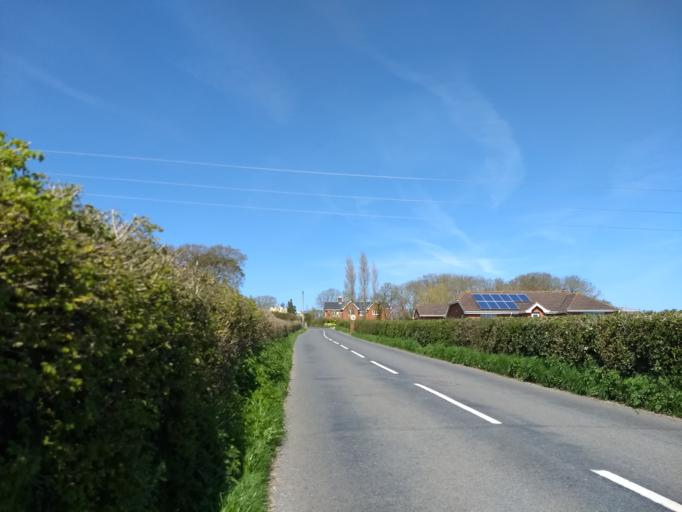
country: GB
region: England
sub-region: Isle of Wight
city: Northwood
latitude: 50.7396
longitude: -1.3345
